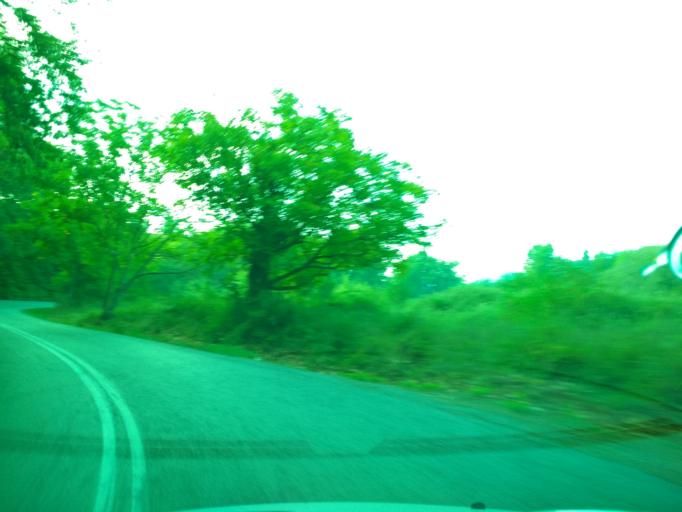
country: GR
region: Central Greece
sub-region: Nomos Evvoias
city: Prokopion
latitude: 38.7626
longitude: 23.4781
